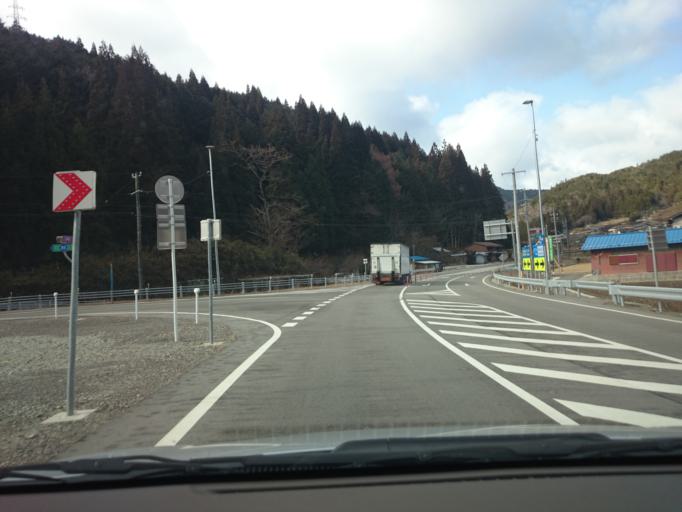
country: JP
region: Gifu
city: Gujo
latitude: 35.7406
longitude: 137.1219
